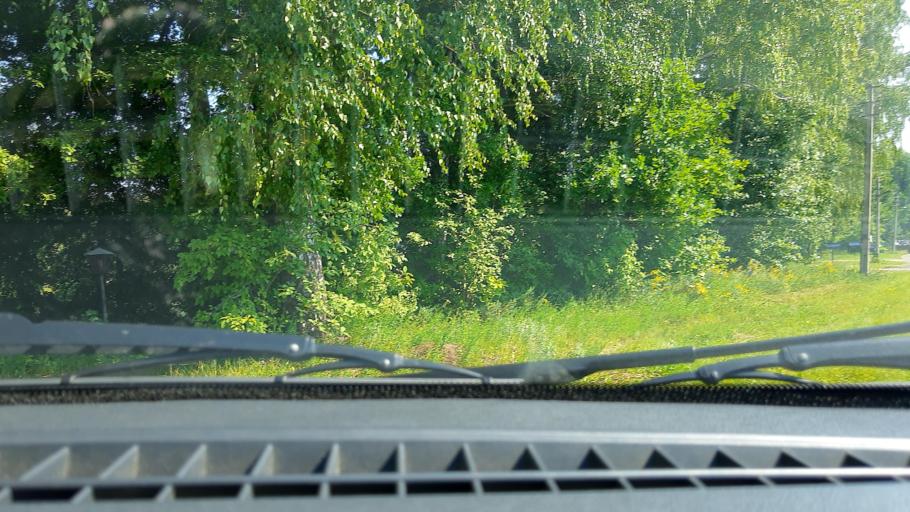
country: RU
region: Bashkortostan
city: Mikhaylovka
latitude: 54.8325
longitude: 55.8557
